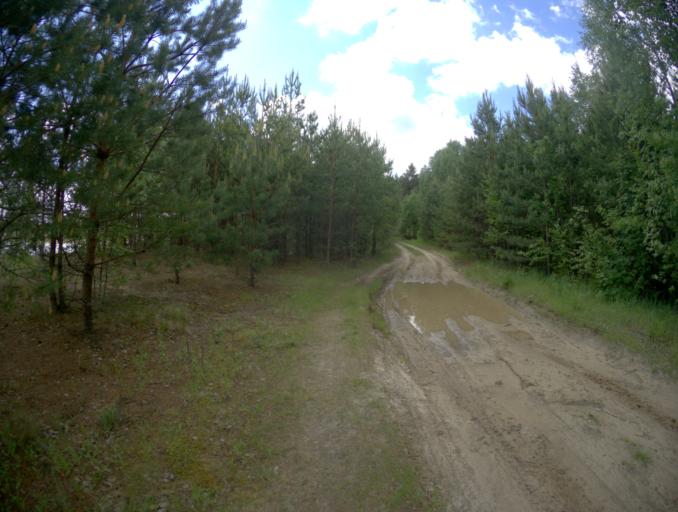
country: RU
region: Vladimir
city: Velikodvorskiy
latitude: 55.2334
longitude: 40.6325
